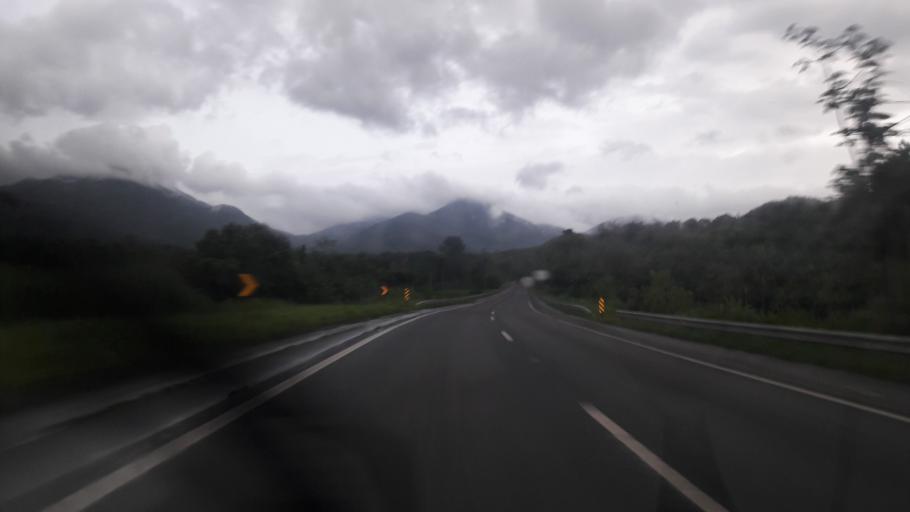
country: BR
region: Sao Paulo
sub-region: Cajati
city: Cajati
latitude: -24.7801
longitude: -48.1934
